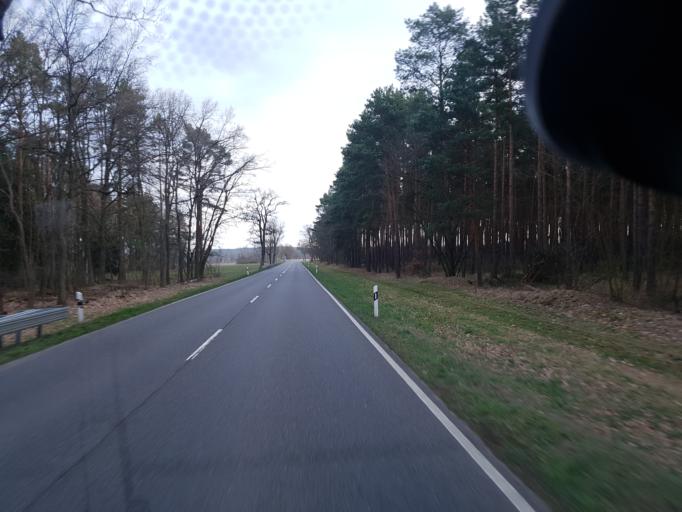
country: DE
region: Brandenburg
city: Schlepzig
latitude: 51.9801
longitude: 13.9624
